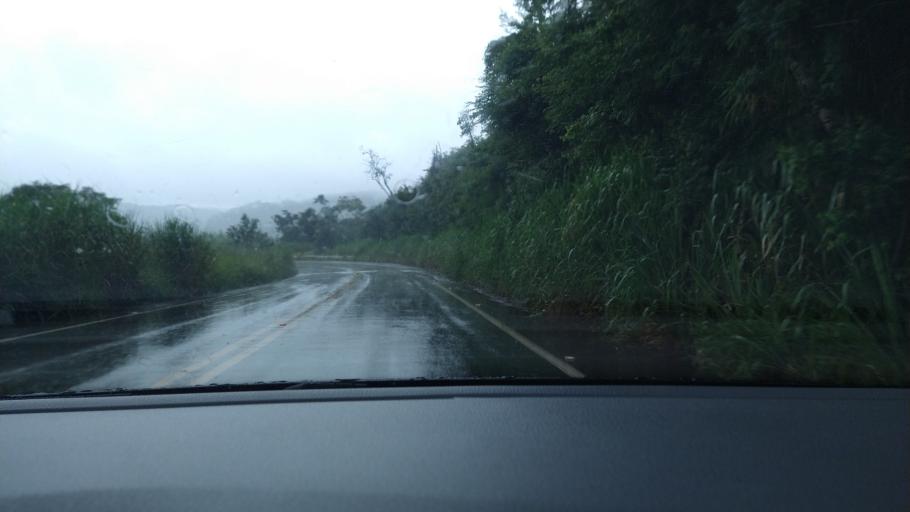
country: BR
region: Minas Gerais
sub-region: Ponte Nova
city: Ponte Nova
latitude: -20.5550
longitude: -42.8734
